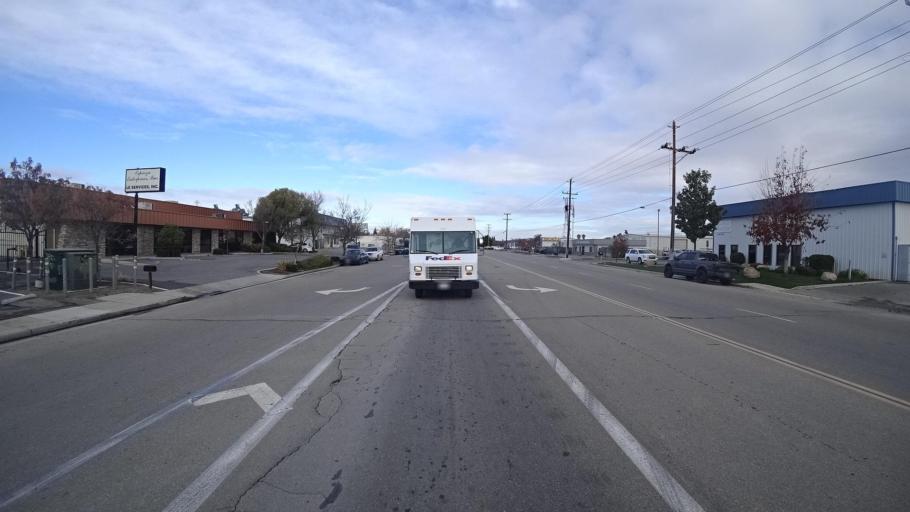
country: US
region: California
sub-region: Kern County
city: Greenacres
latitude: 35.3946
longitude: -119.0744
